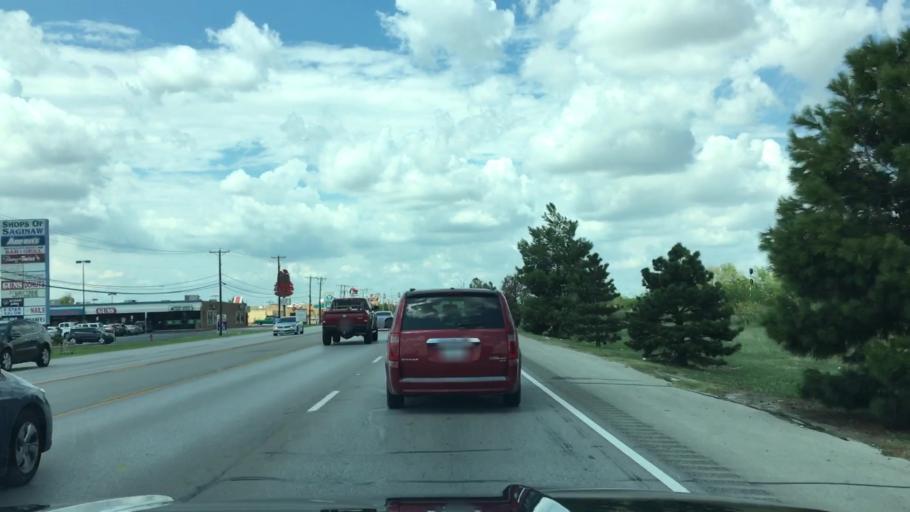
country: US
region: Texas
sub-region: Tarrant County
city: Saginaw
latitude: 32.8756
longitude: -97.3770
